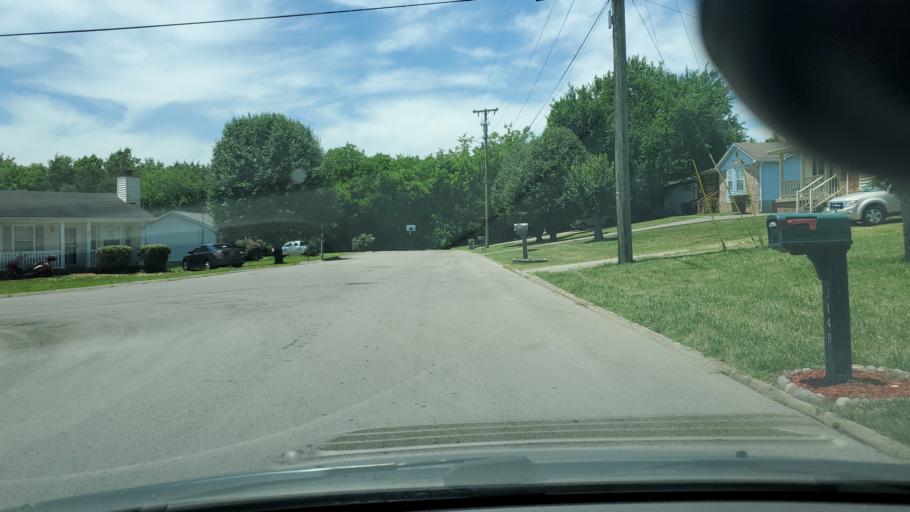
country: US
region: Tennessee
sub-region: Davidson County
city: Nashville
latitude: 36.2222
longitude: -86.7559
